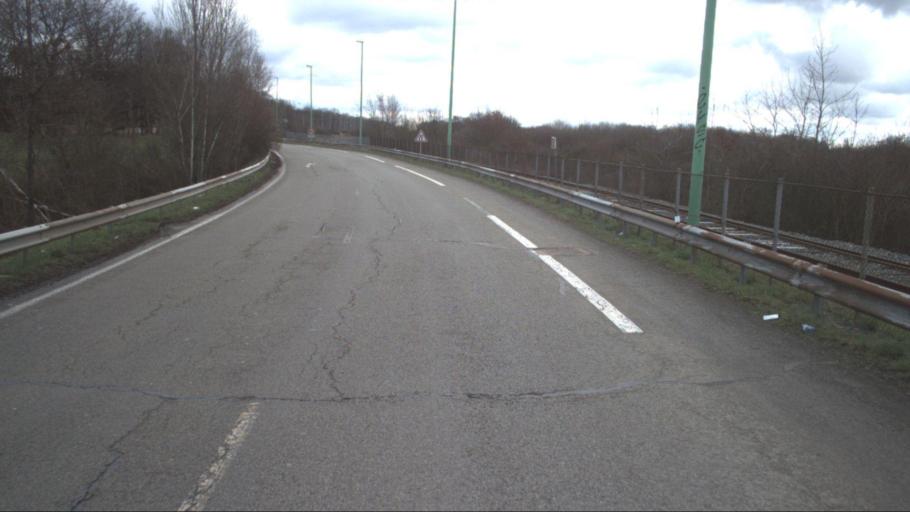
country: FR
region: Ile-de-France
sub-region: Departement des Yvelines
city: Saint-Cyr-l'Ecole
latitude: 48.7930
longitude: 2.0778
